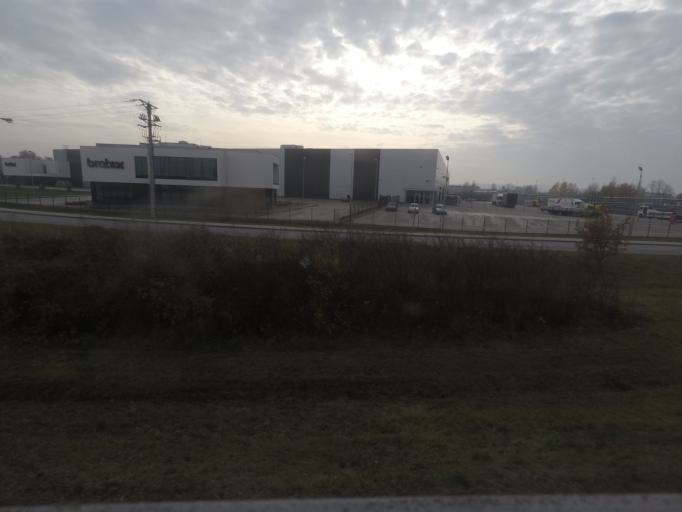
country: PL
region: Subcarpathian Voivodeship
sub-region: Powiat debicki
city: Debica
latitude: 50.0618
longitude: 21.4439
